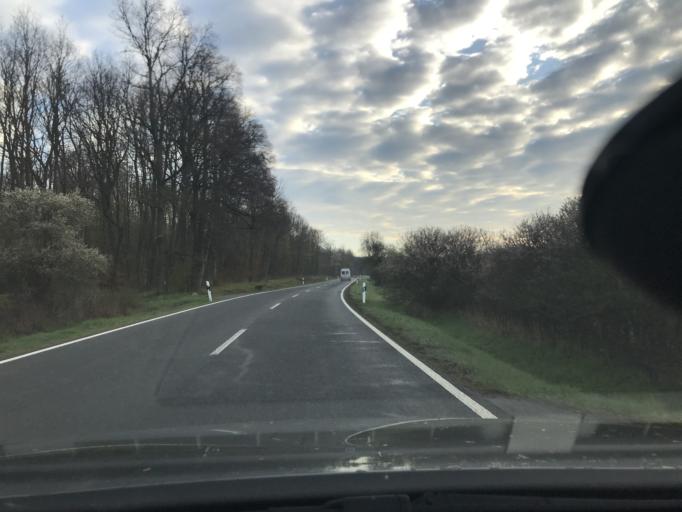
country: DE
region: Thuringia
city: Menteroda
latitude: 51.2816
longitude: 10.5383
